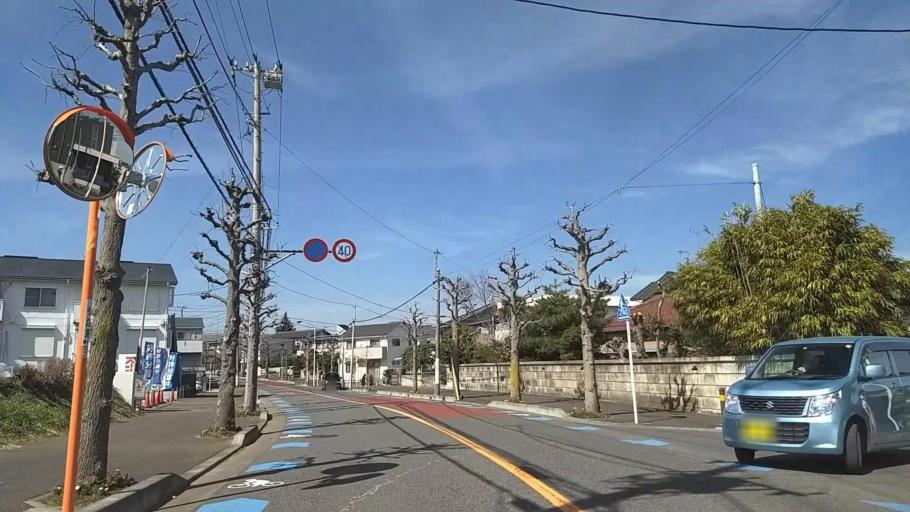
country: JP
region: Kanagawa
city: Fujisawa
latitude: 35.4018
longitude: 139.4722
